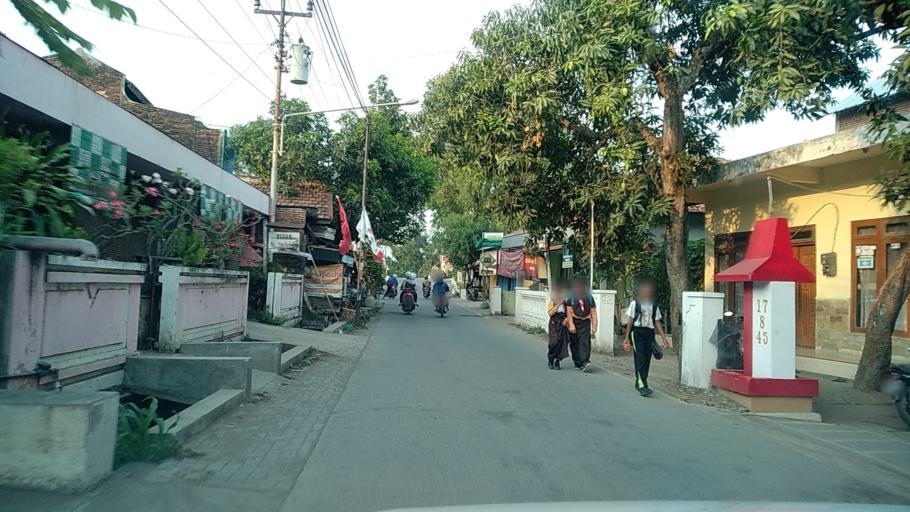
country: ID
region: Central Java
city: Semarang
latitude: -6.9719
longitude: 110.3043
